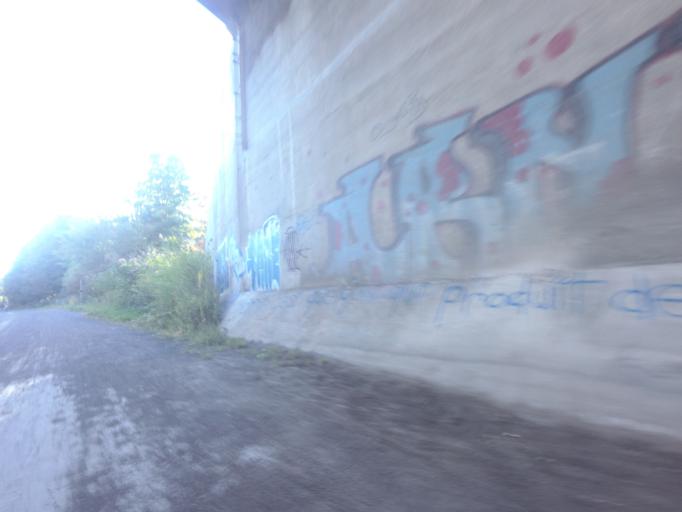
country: CA
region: Quebec
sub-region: Laurentides
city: Saint-Jerome
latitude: 45.8116
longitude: -74.0260
